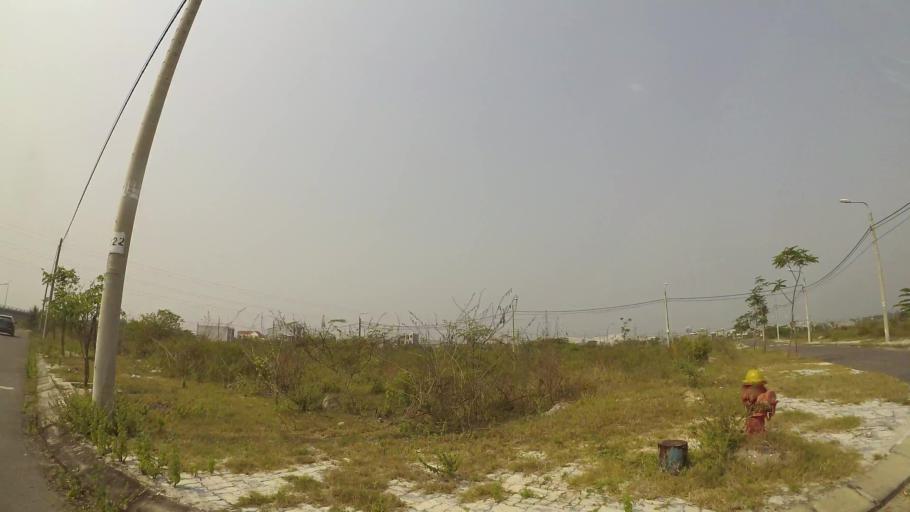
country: VN
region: Da Nang
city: Cam Le
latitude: 15.9704
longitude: 108.2157
